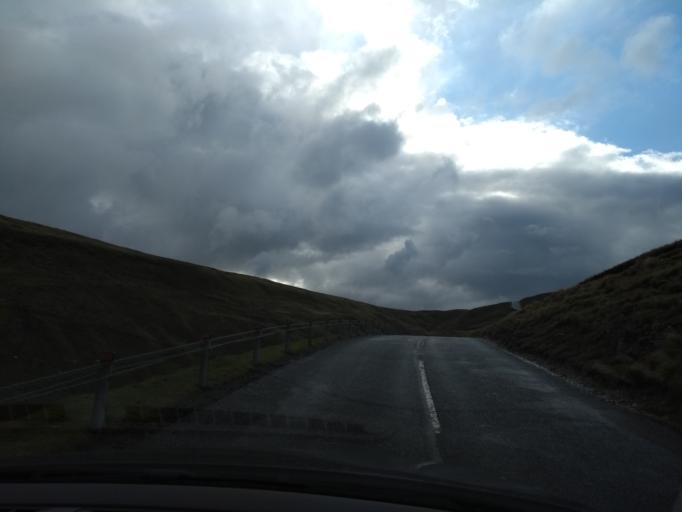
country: GB
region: England
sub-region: Cumbria
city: Kirkby Stephen
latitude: 54.3610
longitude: -2.1940
